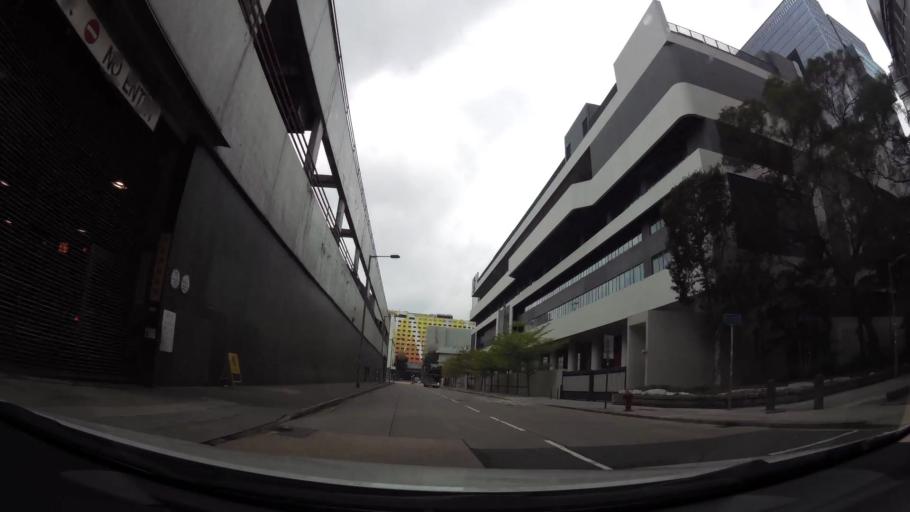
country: HK
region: Kowloon City
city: Kowloon
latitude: 22.3245
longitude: 114.2076
